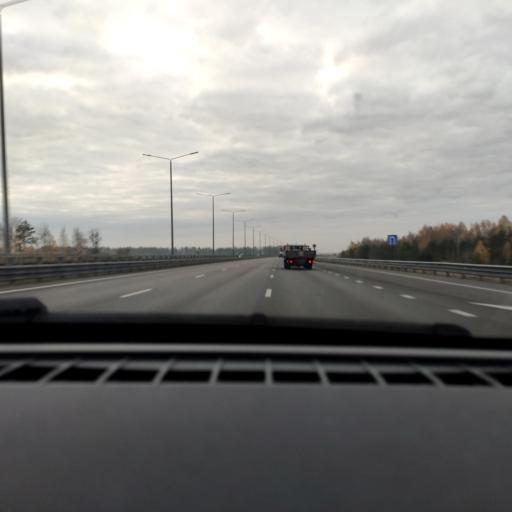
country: RU
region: Voronezj
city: Somovo
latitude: 51.7857
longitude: 39.2860
